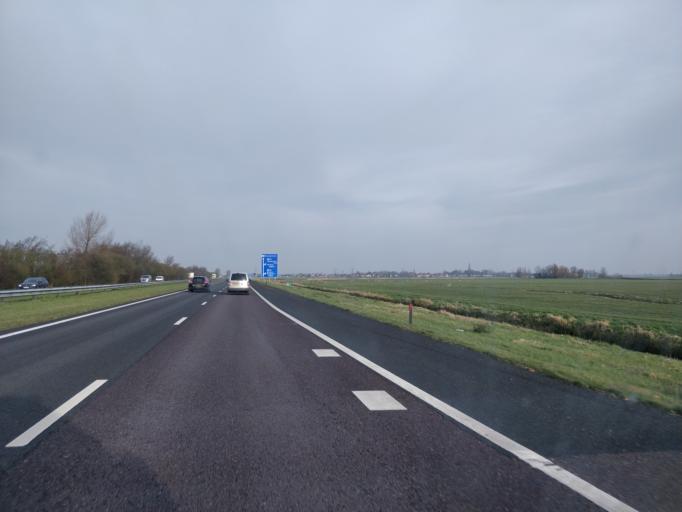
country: NL
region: Friesland
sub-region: Gemeente Leeuwarden
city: Wirdum
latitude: 53.1345
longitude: 5.8012
